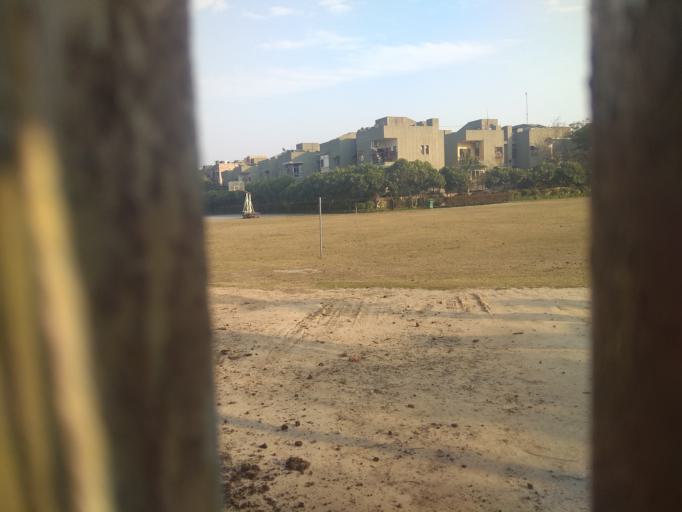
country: IN
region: NCT
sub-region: West Delhi
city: Nangloi Jat
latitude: 28.6416
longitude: 77.0649
